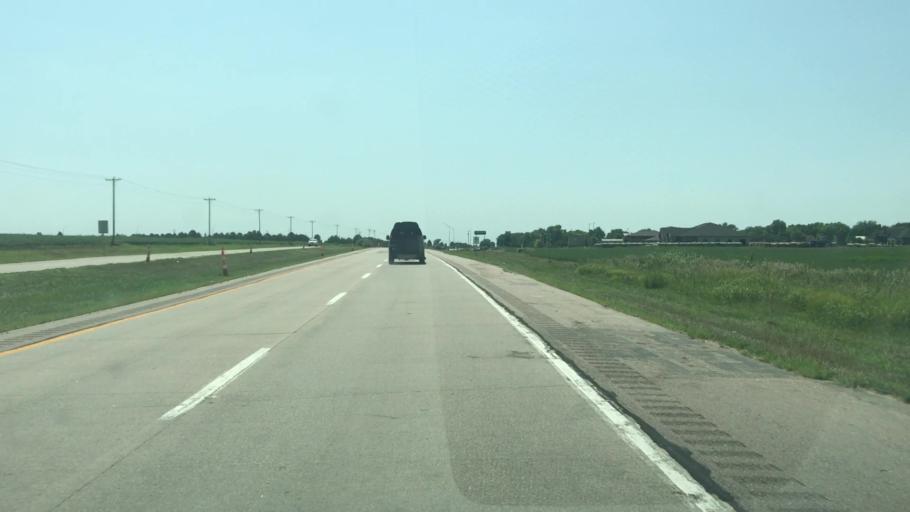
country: US
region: Nebraska
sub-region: Adams County
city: Hastings
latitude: 40.6454
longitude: -98.3824
